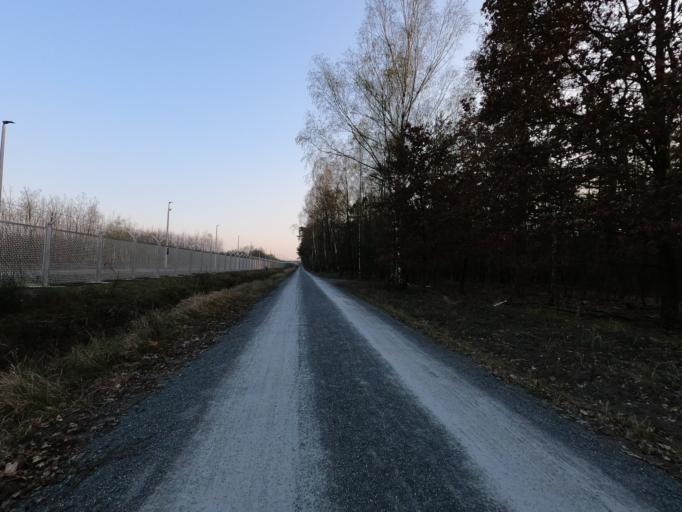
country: DE
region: Hesse
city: Kelsterbach
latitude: 50.0101
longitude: 8.5221
